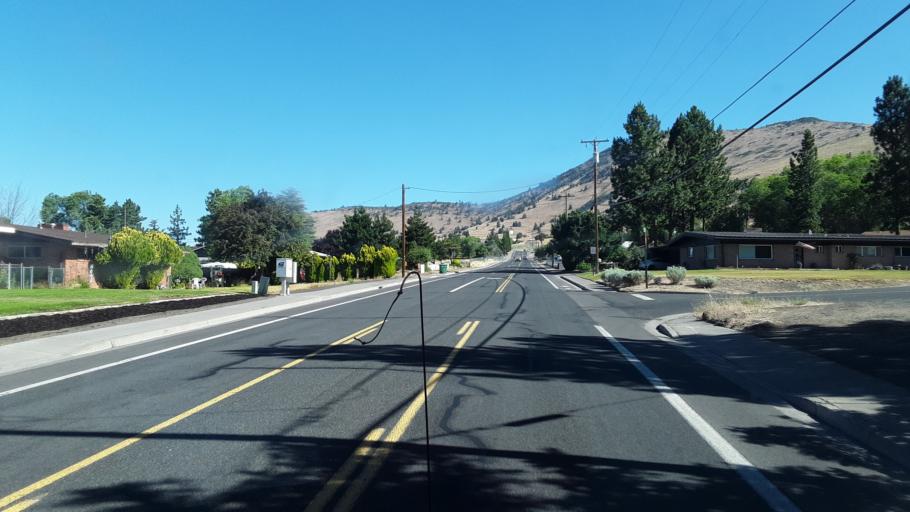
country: US
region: Oregon
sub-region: Klamath County
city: Altamont
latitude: 42.2161
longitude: -121.7129
